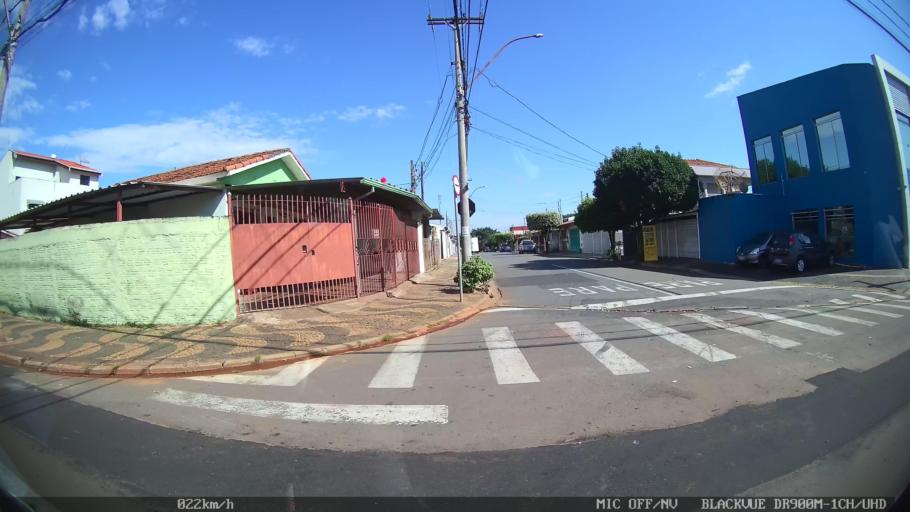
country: BR
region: Sao Paulo
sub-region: Santa Barbara D'Oeste
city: Santa Barbara d'Oeste
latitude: -22.7351
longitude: -47.3805
